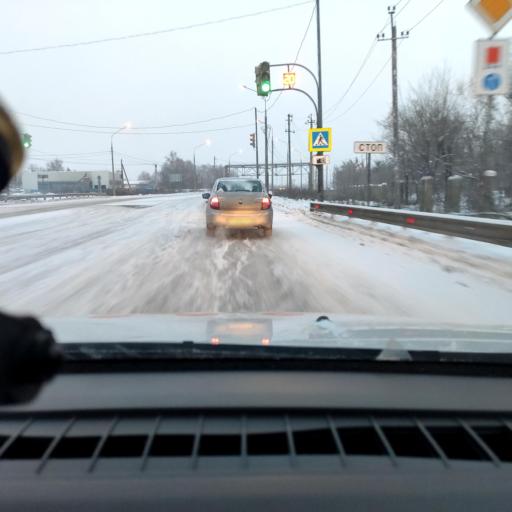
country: RU
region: Samara
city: Otradnyy
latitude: 53.3730
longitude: 51.3702
